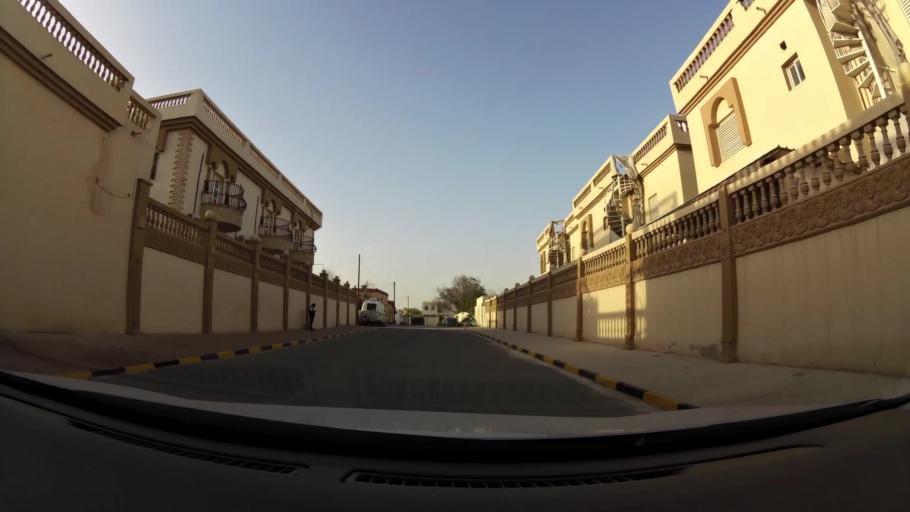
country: QA
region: Baladiyat ar Rayyan
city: Ar Rayyan
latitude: 25.3233
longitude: 51.4581
